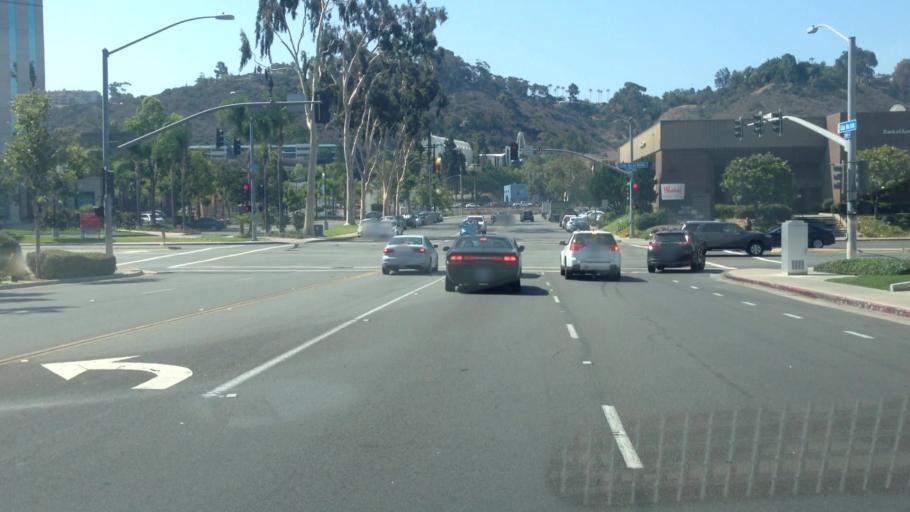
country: US
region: California
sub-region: San Diego County
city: San Diego
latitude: 32.7714
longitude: -117.1444
